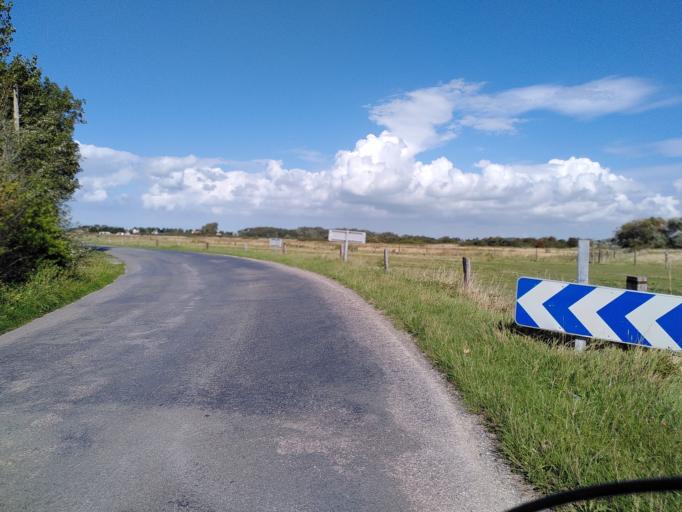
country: FR
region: Nord-Pas-de-Calais
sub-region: Departement du Pas-de-Calais
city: Oye-Plage
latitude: 50.9897
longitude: 2.0407
